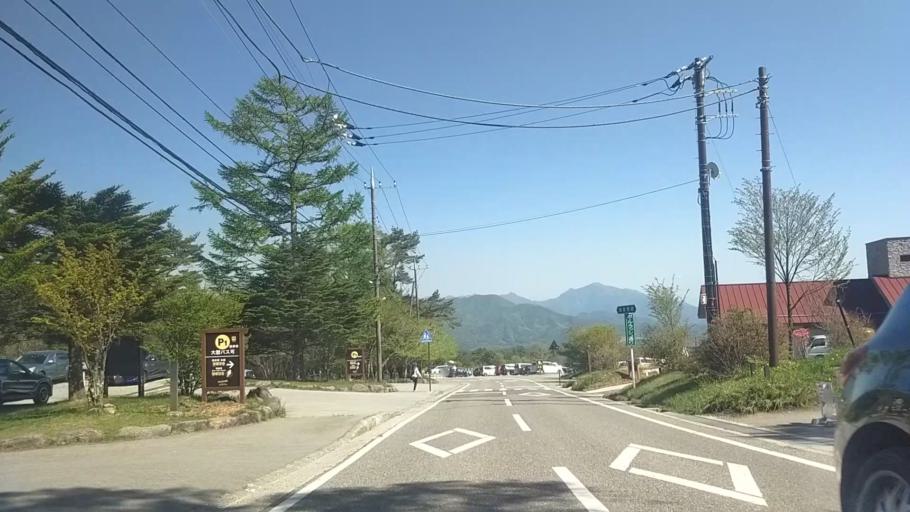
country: JP
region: Yamanashi
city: Nirasaki
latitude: 35.9256
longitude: 138.4205
